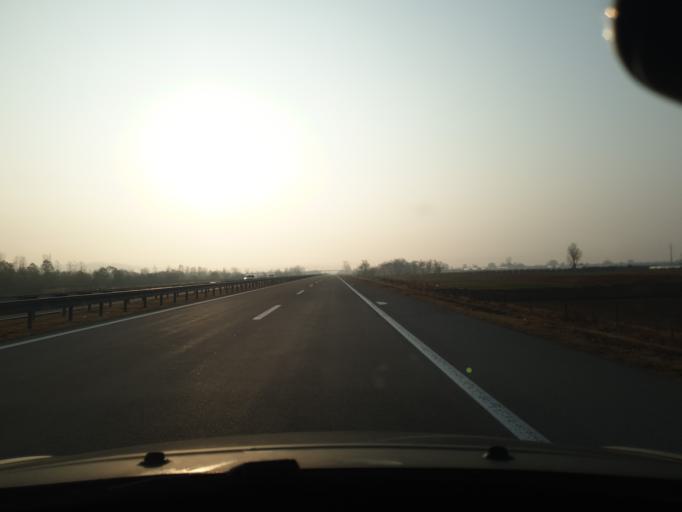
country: RS
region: Central Serbia
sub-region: Jablanicki Okrug
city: Leskovac
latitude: 43.0515
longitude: 21.9812
